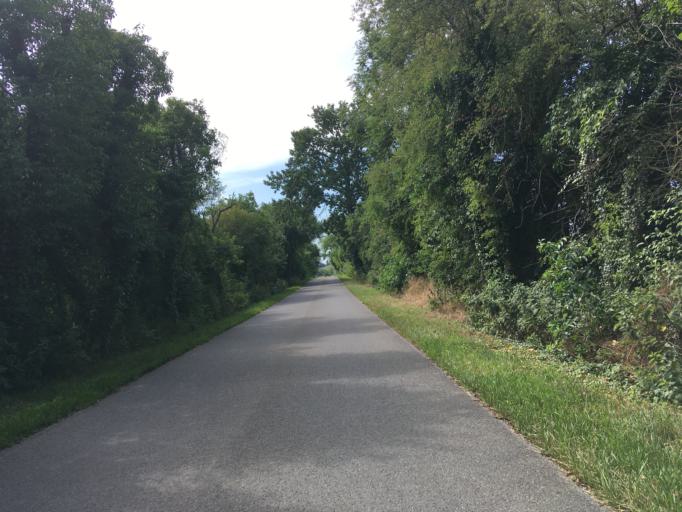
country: DE
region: Brandenburg
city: Zichow
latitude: 53.2126
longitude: 14.0453
